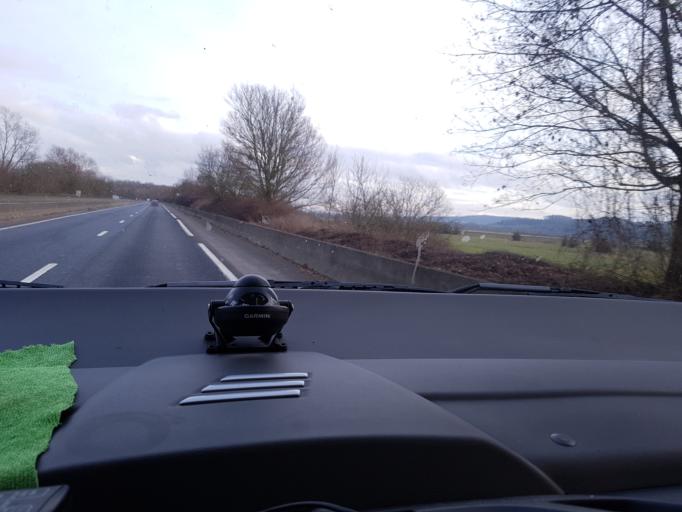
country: FR
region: Champagne-Ardenne
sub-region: Departement des Ardennes
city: Balan
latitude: 49.6849
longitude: 4.9560
